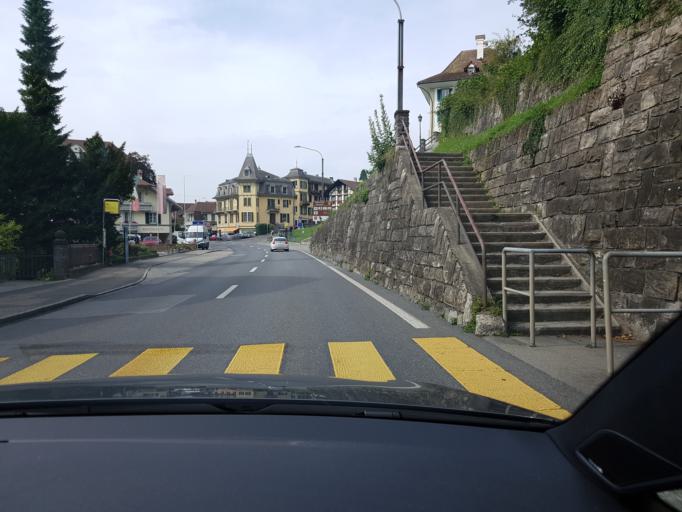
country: CH
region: Bern
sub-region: Thun District
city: Hilterfingen
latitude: 46.7332
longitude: 7.6618
